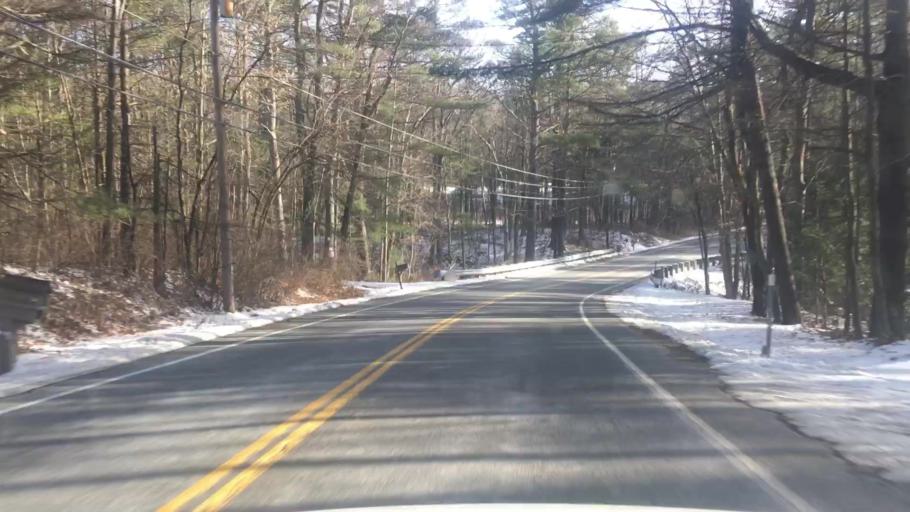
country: US
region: New Hampshire
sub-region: Merrimack County
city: Canterbury
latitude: 43.3008
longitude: -71.5645
